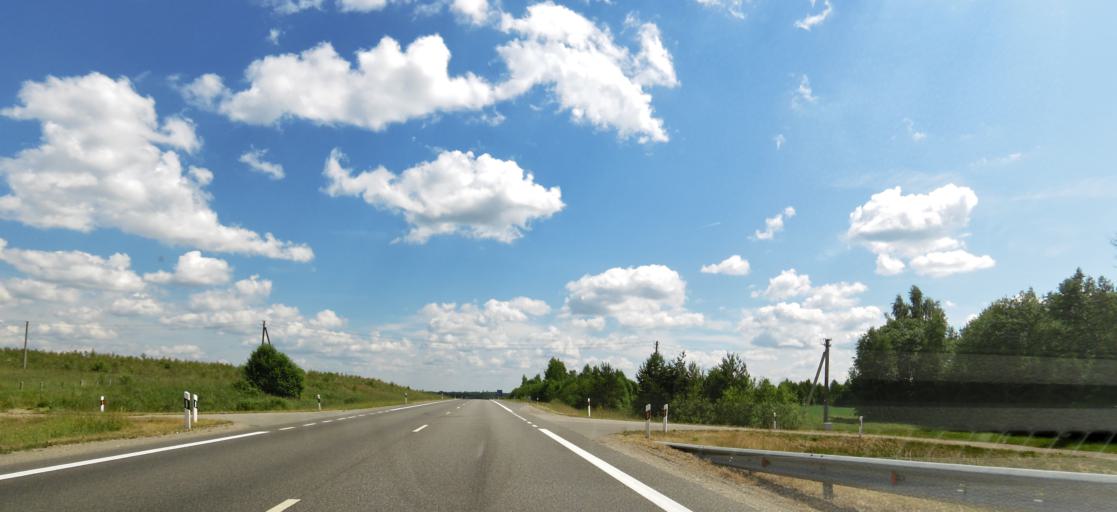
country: LT
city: Skaidiskes
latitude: 54.5656
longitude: 25.6410
